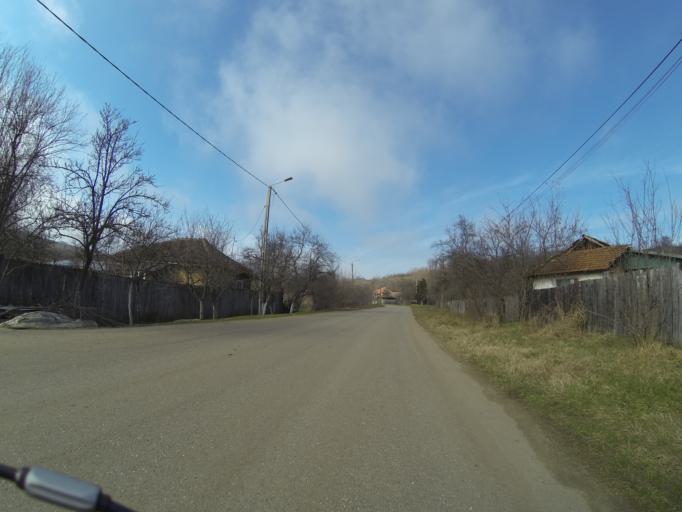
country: RO
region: Mehedinti
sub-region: Comuna Poroina Mare
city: Poroina Mare
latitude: 44.4951
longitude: 22.9880
